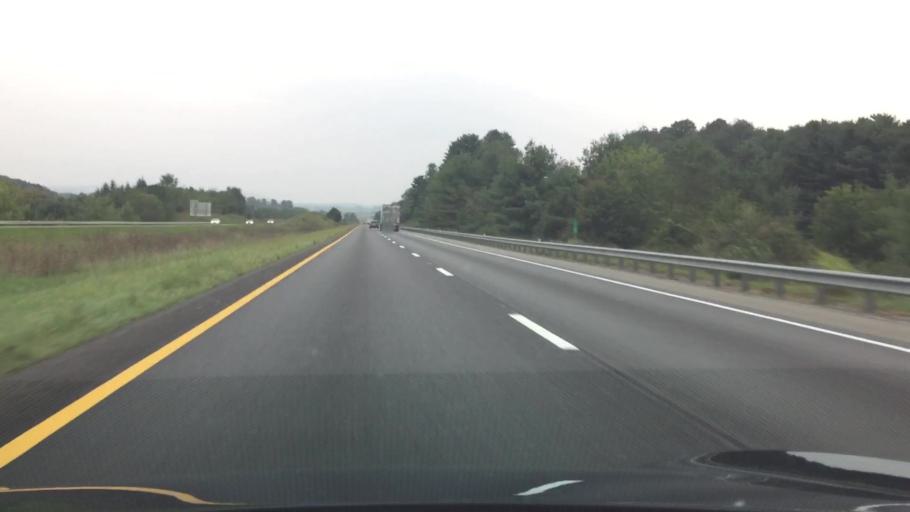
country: US
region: Virginia
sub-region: Montgomery County
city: Christiansburg
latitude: 37.1119
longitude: -80.4415
